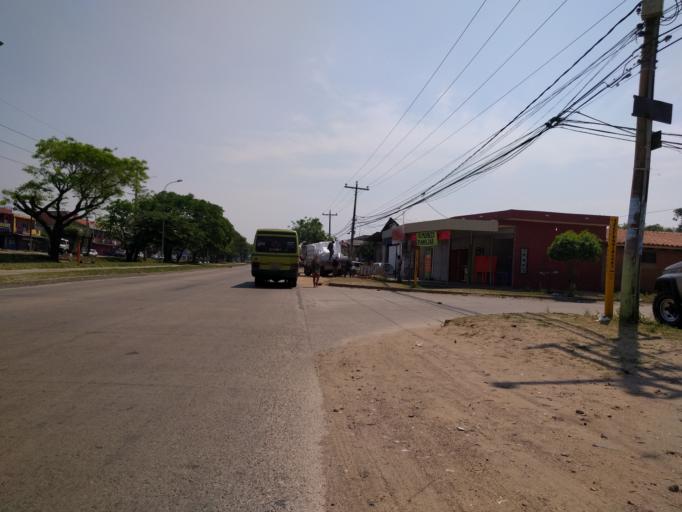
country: BO
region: Santa Cruz
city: Santa Cruz de la Sierra
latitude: -17.8013
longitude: -63.1509
